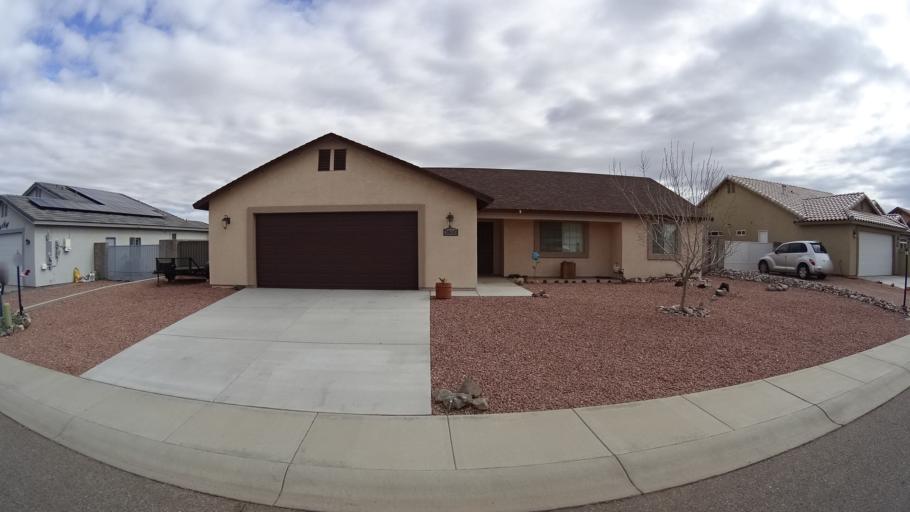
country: US
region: Arizona
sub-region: Mohave County
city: New Kingman-Butler
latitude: 35.2341
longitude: -114.0016
